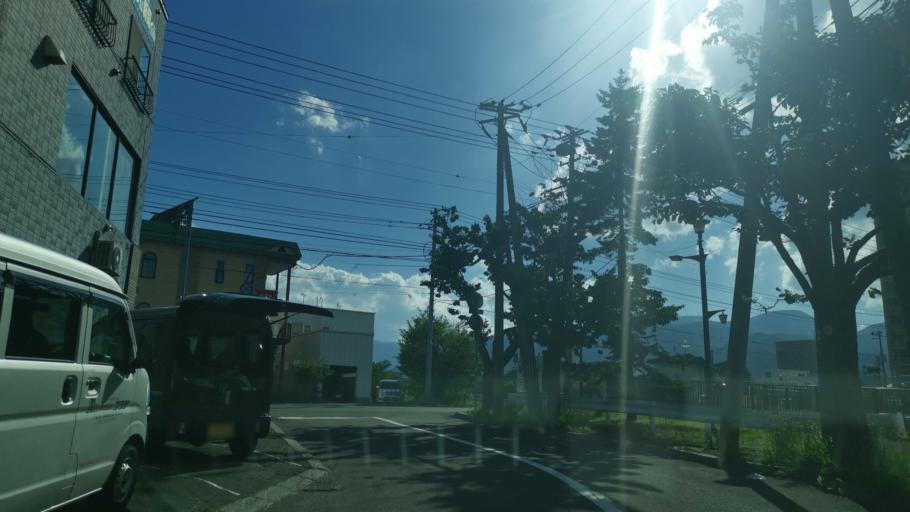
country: JP
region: Hokkaido
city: Sapporo
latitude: 43.0731
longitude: 141.2859
